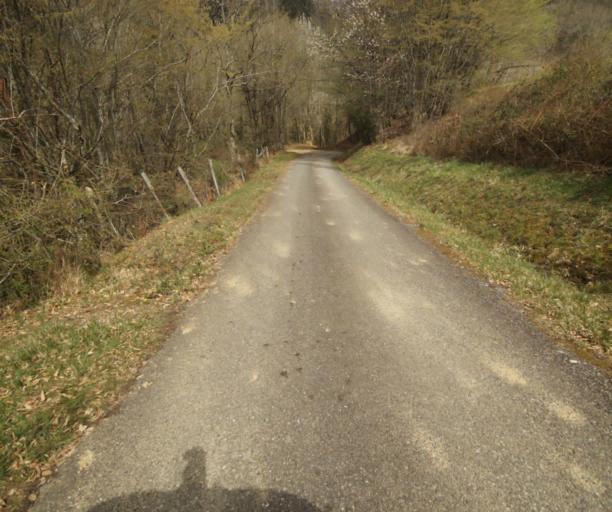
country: FR
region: Limousin
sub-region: Departement de la Correze
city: Sainte-Fortunade
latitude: 45.1858
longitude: 1.8531
